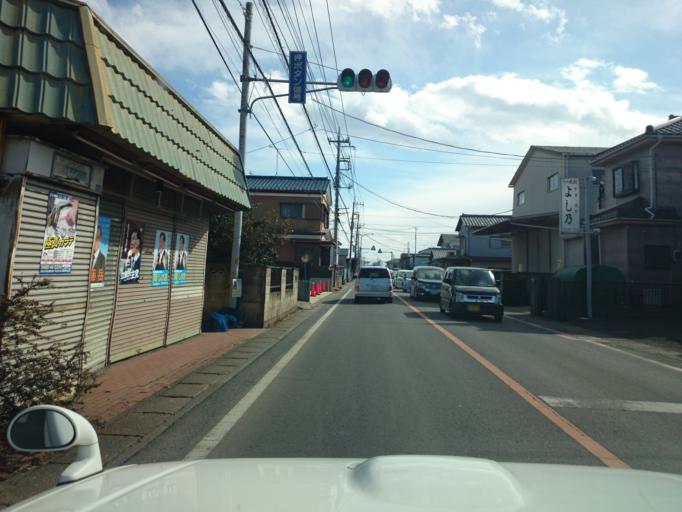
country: JP
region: Saitama
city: Sugito
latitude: 36.0394
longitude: 139.7036
